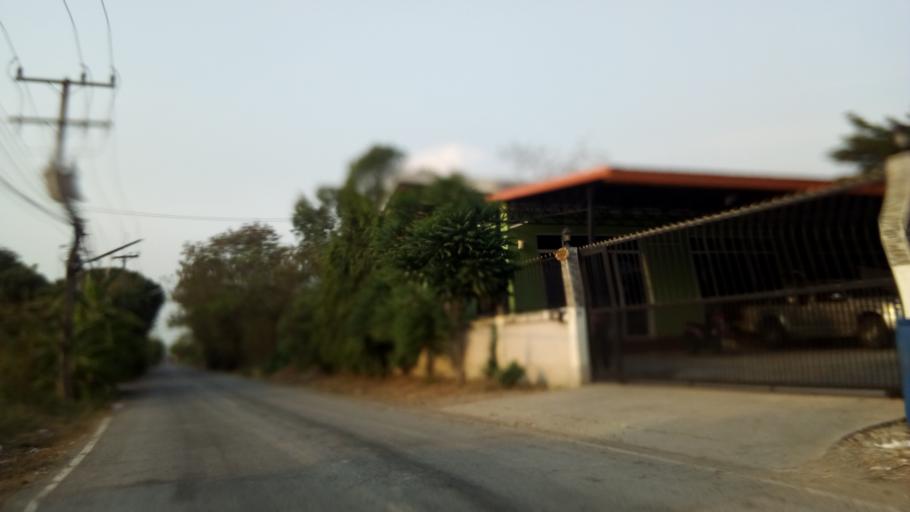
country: TH
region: Pathum Thani
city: Nong Suea
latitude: 14.0578
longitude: 100.8313
